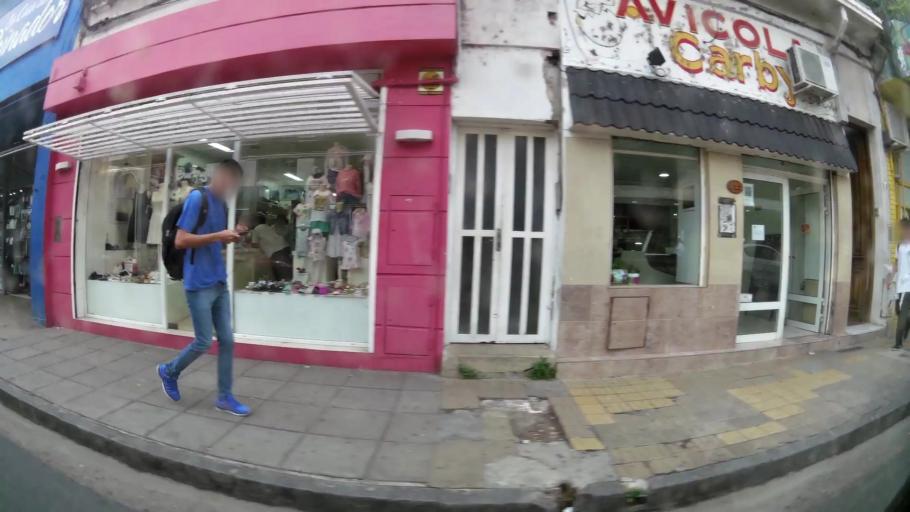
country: AR
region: Buenos Aires
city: San Nicolas de los Arroyos
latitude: -33.3289
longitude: -60.2173
